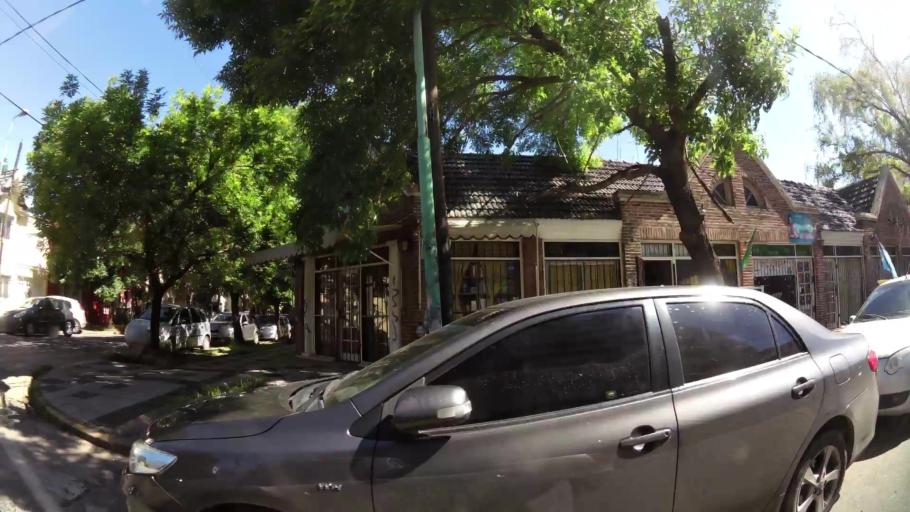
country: AR
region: Buenos Aires
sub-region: Partido de Lomas de Zamora
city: Lomas de Zamora
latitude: -34.7552
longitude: -58.4046
